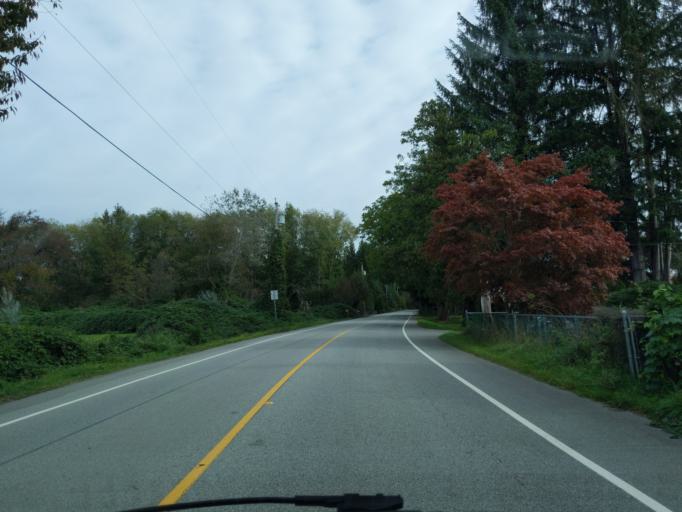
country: CA
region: British Columbia
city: Maple Ridge
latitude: 49.2057
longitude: -122.6205
